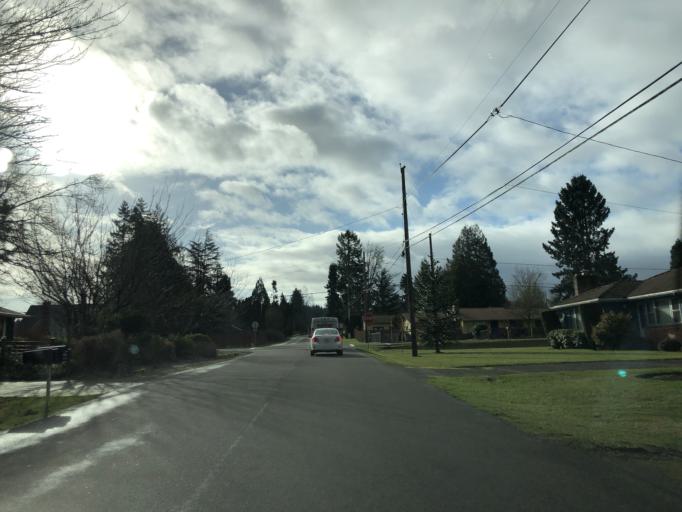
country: US
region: Oregon
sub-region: Washington County
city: Tigard
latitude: 45.4246
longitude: -122.7857
